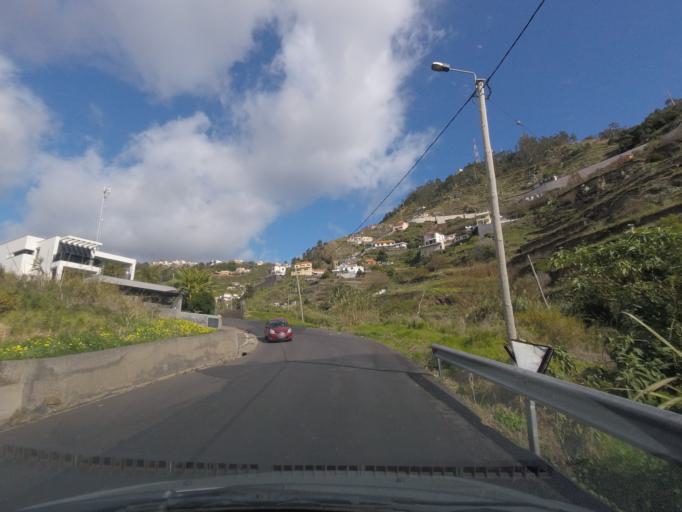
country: PT
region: Madeira
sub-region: Ribeira Brava
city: Campanario
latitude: 32.6601
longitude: -17.0104
